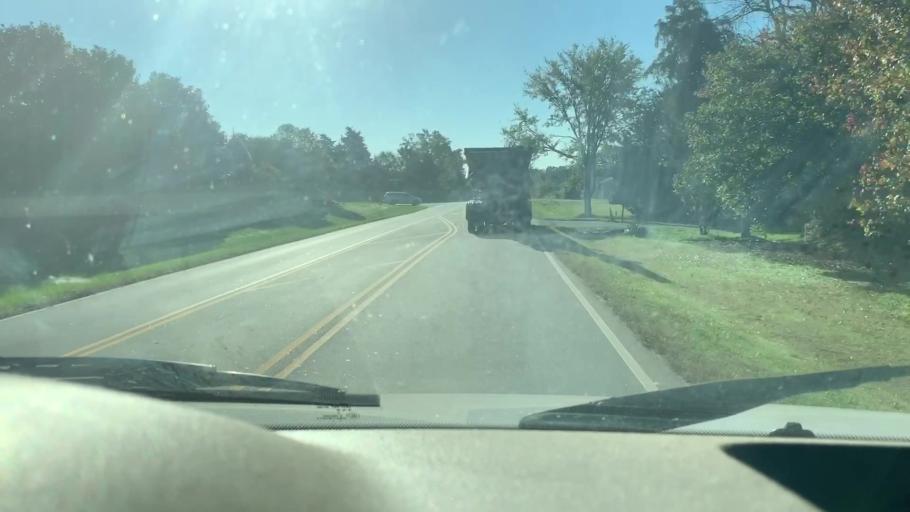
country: US
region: North Carolina
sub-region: Mecklenburg County
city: Huntersville
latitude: 35.4158
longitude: -80.7423
